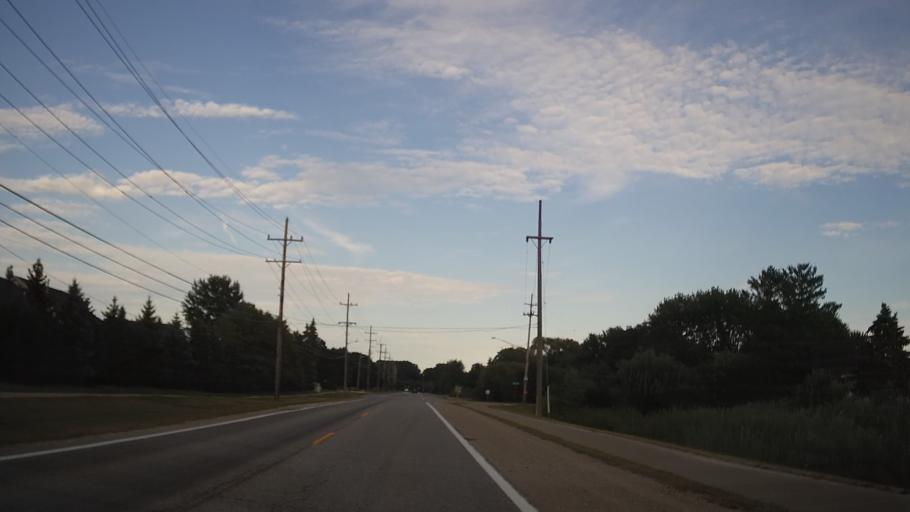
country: US
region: Michigan
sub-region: Macomb County
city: Clinton
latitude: 42.5985
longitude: -82.9252
